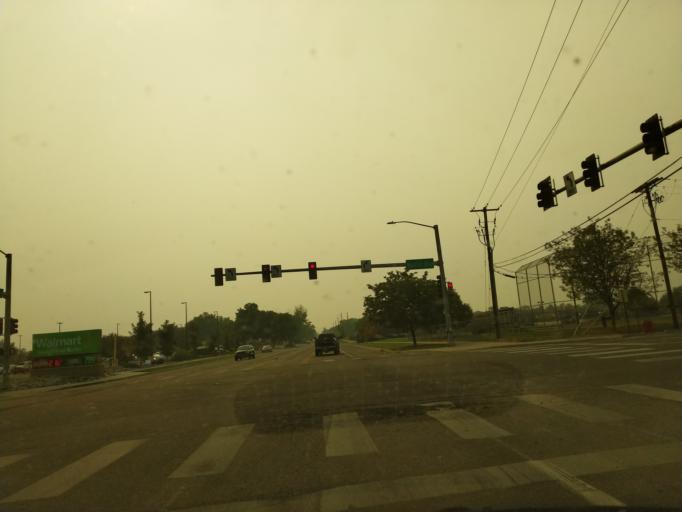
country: US
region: Colorado
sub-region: Mesa County
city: Fruitvale
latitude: 39.0846
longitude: -108.4729
